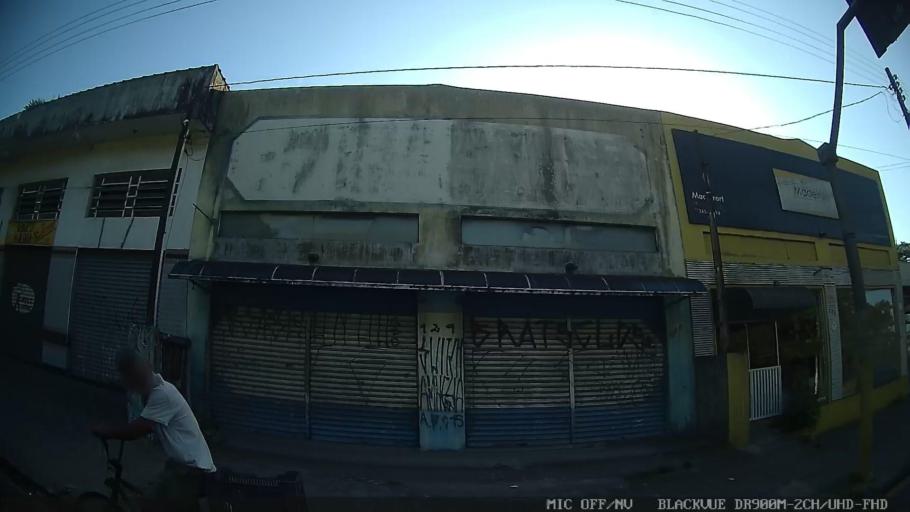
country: BR
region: Sao Paulo
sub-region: Peruibe
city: Peruibe
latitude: -24.2713
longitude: -46.9558
